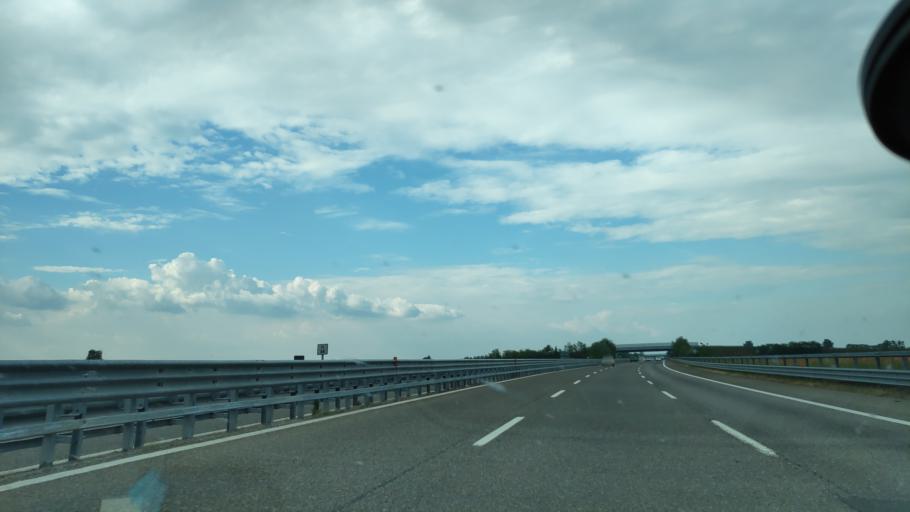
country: IT
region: Lombardy
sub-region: Provincia di Pavia
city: Pieve Albignola
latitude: 45.1273
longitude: 8.9788
